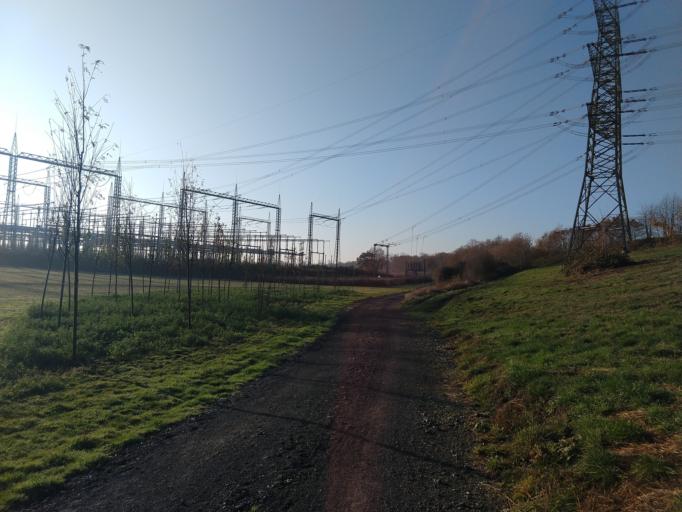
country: DE
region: North Rhine-Westphalia
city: Wesseling
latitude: 50.7972
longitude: 6.9703
